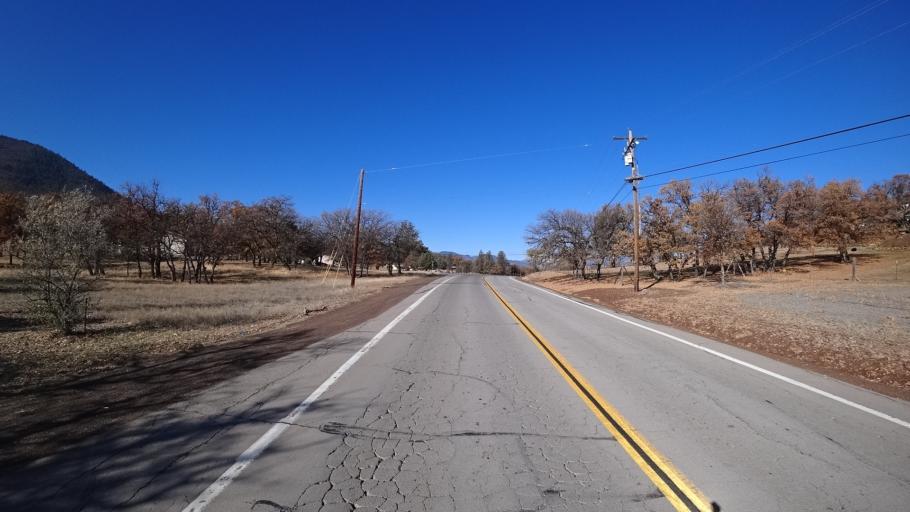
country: US
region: California
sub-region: Siskiyou County
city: Montague
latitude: 41.8814
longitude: -122.4833
